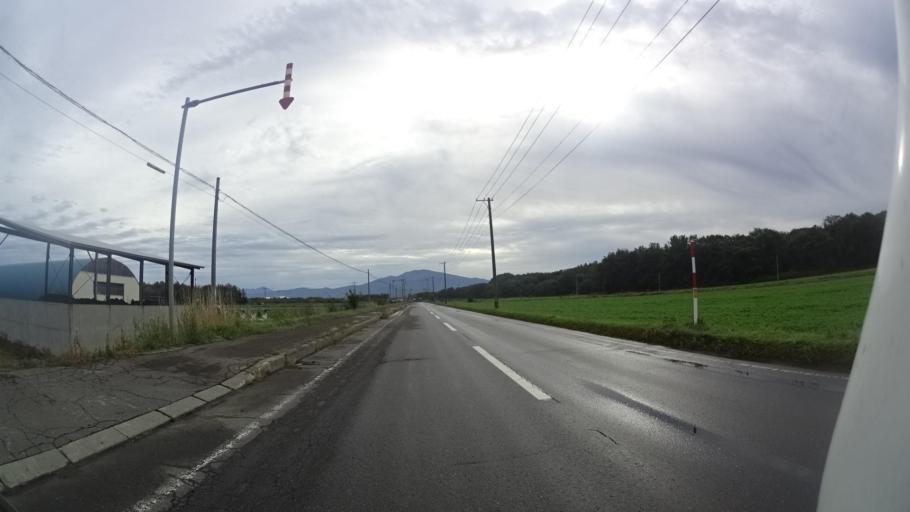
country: JP
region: Hokkaido
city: Abashiri
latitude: 43.8696
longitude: 144.6390
